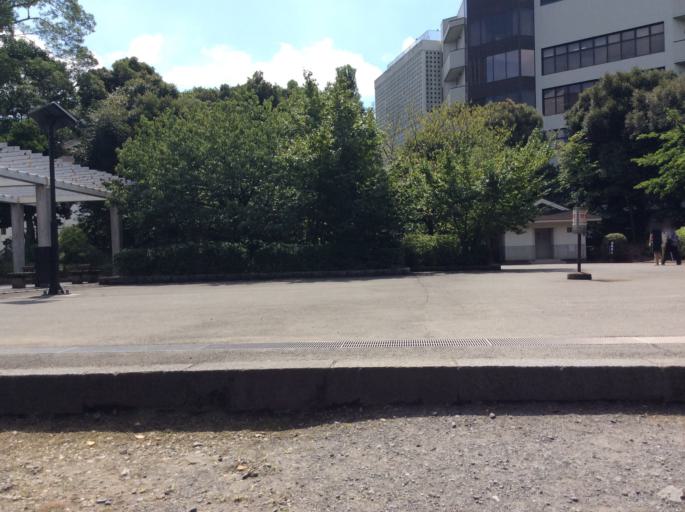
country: JP
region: Tokyo
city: Tokyo
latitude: 35.6924
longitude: 139.7525
